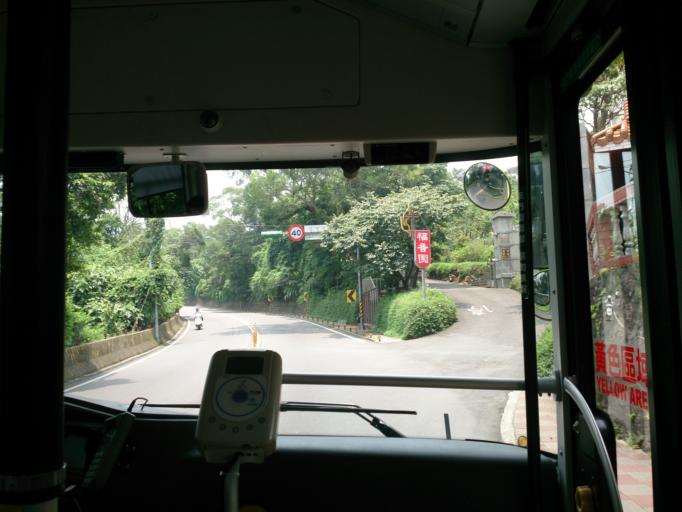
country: TW
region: Taipei
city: Taipei
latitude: 25.1109
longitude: 121.5491
